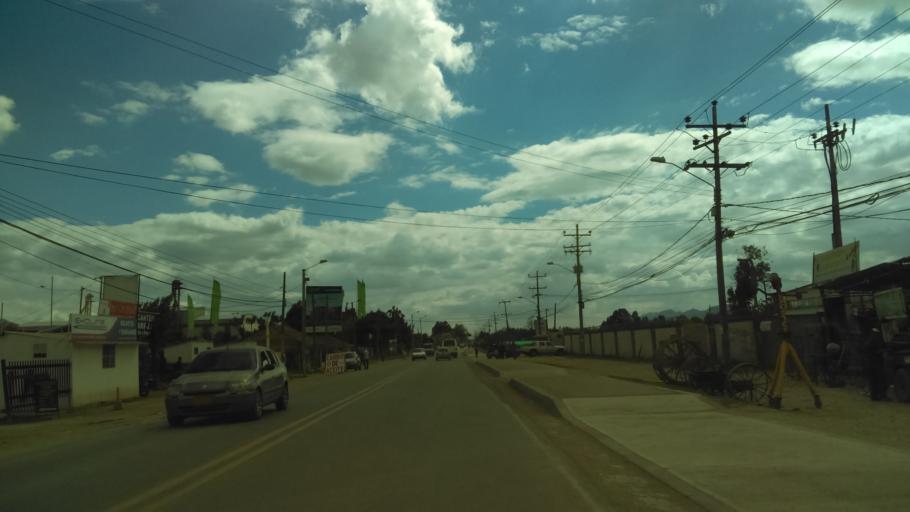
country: CO
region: Cundinamarca
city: Cajica
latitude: 4.9321
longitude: -74.0207
